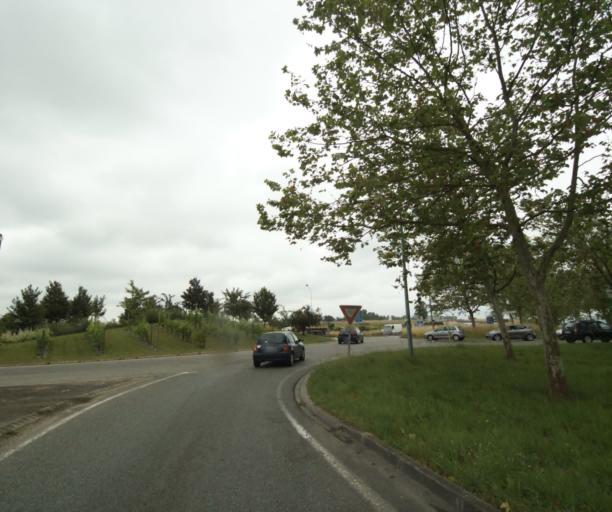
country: FR
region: Midi-Pyrenees
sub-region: Departement du Tarn-et-Garonne
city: Bressols
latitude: 43.9928
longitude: 1.3379
